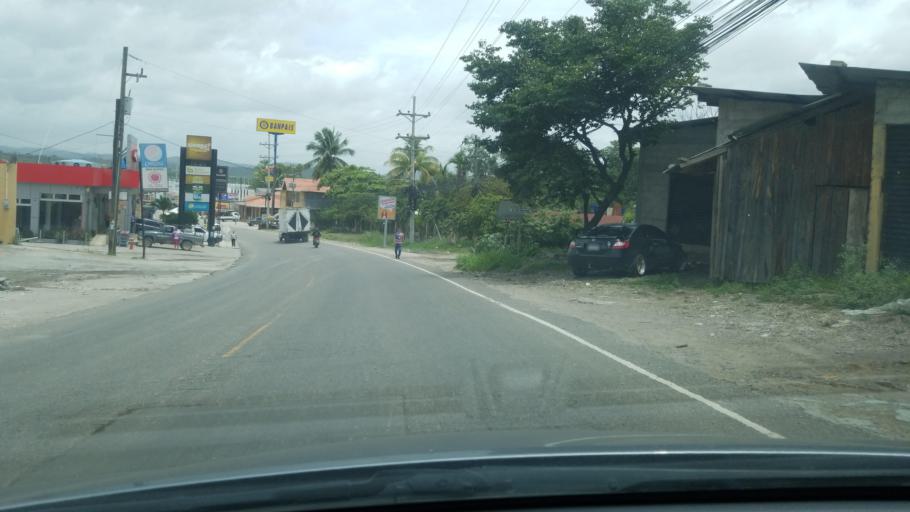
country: HN
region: Copan
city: Cucuyagua
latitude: 14.6551
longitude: -88.8750
